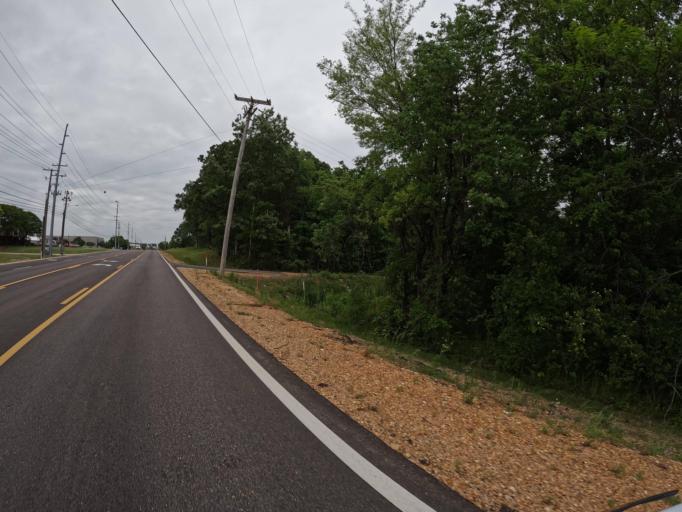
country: US
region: Mississippi
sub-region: Lee County
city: Tupelo
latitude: 34.2690
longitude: -88.7643
